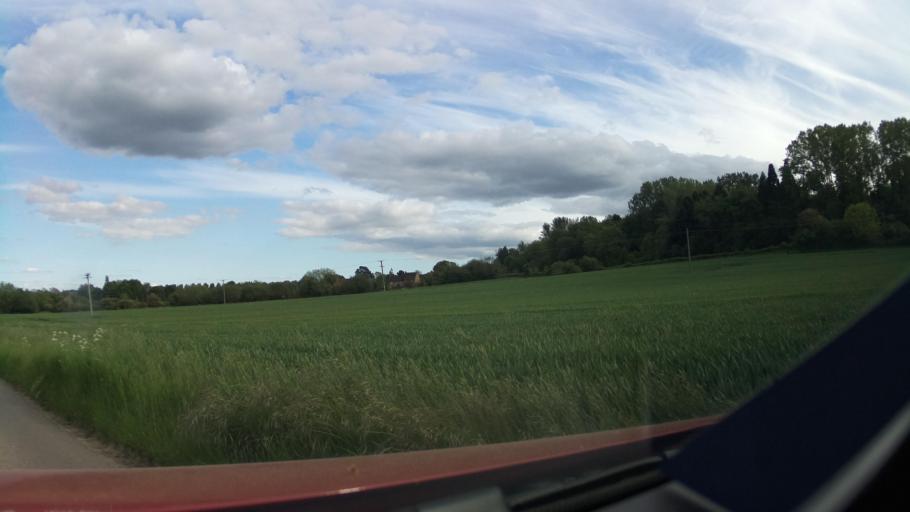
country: GB
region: England
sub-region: Gloucestershire
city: Moreton in Marsh
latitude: 52.0238
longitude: -1.7124
